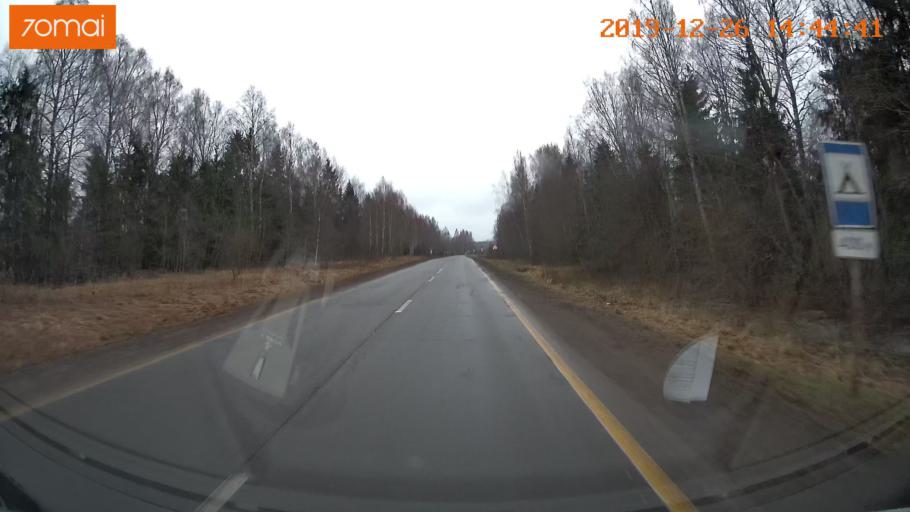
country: RU
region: Jaroslavl
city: Poshekhon'ye
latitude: 58.3449
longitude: 39.0507
